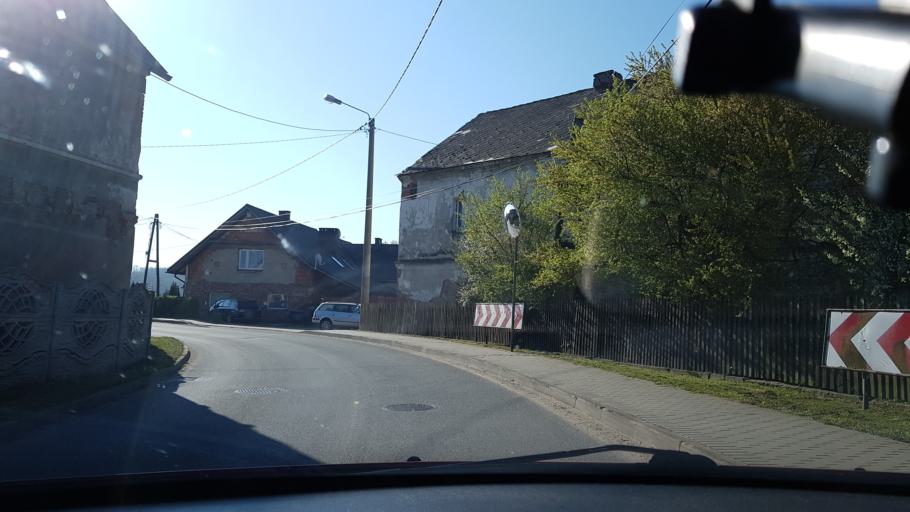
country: PL
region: Opole Voivodeship
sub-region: Powiat nyski
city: Nysa
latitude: 50.4104
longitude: 17.3307
